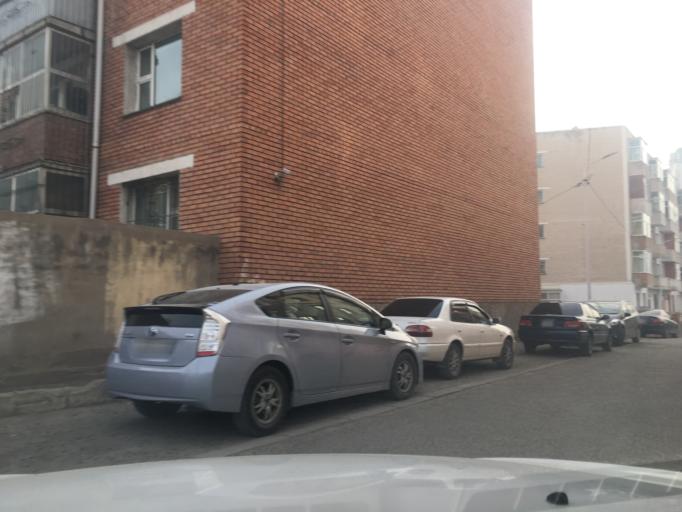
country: MN
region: Ulaanbaatar
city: Ulaanbaatar
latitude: 47.9174
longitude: 106.8705
